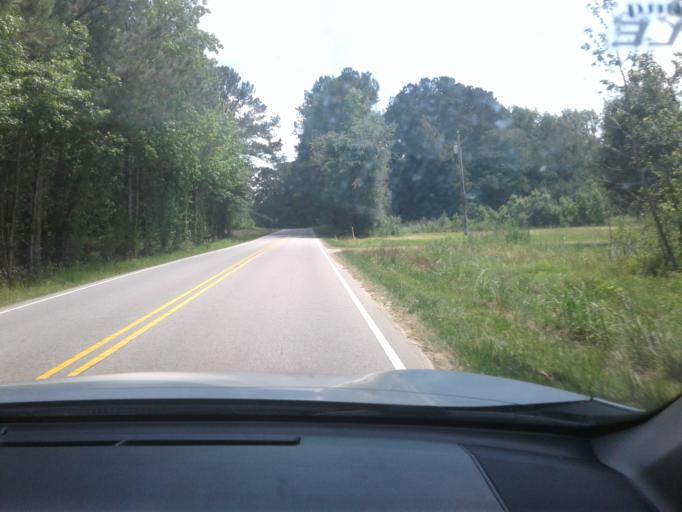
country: US
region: North Carolina
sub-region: Harnett County
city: Erwin
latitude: 35.2432
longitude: -78.6816
